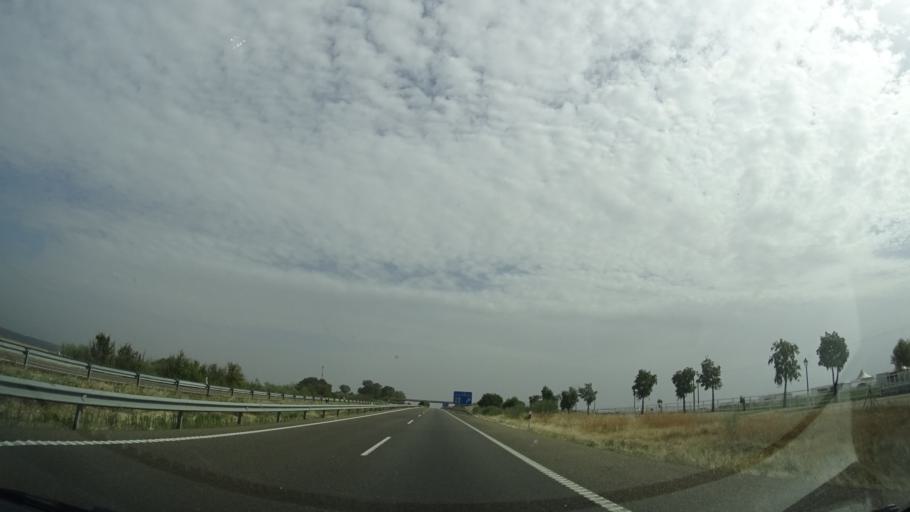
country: ES
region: Extremadura
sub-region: Provincia de Badajoz
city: San Pedro de Merida
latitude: 38.9492
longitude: -6.2087
